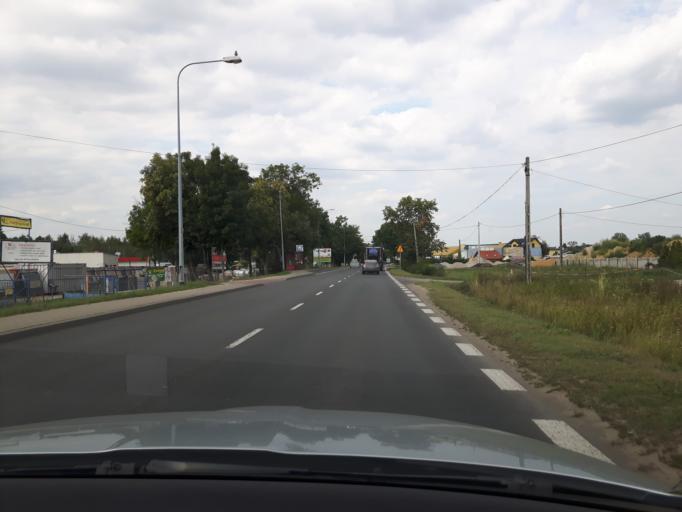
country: PL
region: Masovian Voivodeship
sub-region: Powiat legionowski
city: Stanislawow Pierwszy
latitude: 52.3419
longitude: 21.0286
